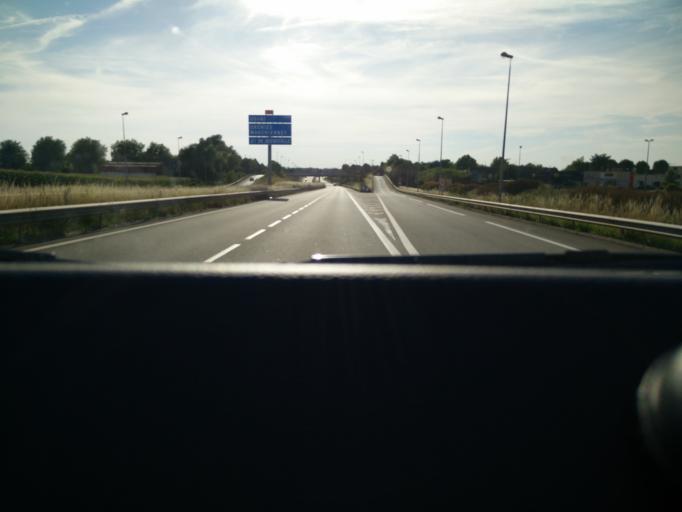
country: FR
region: Nord-Pas-de-Calais
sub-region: Departement du Nord
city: Somain
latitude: 50.3461
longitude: 3.2856
